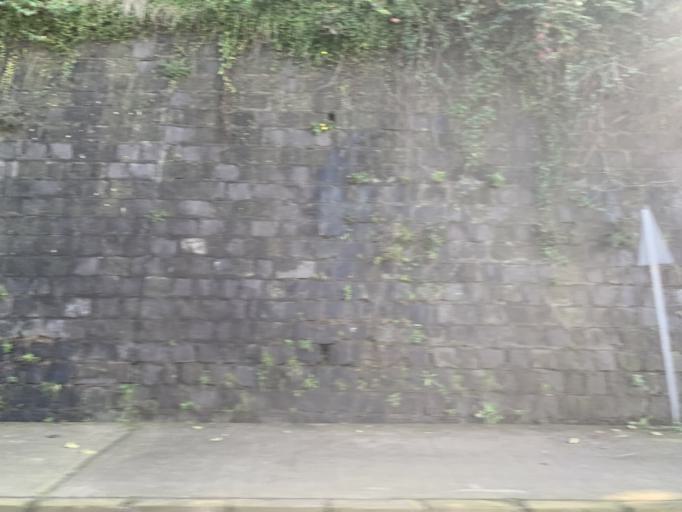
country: TR
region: Trabzon
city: Of
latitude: 40.9286
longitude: 40.2329
